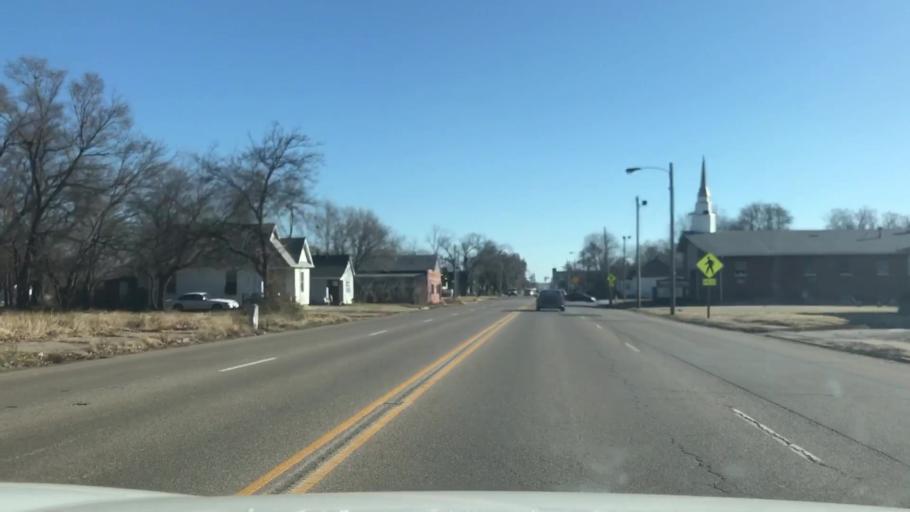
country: US
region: Illinois
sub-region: Saint Clair County
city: East Saint Louis
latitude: 38.6076
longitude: -90.1370
